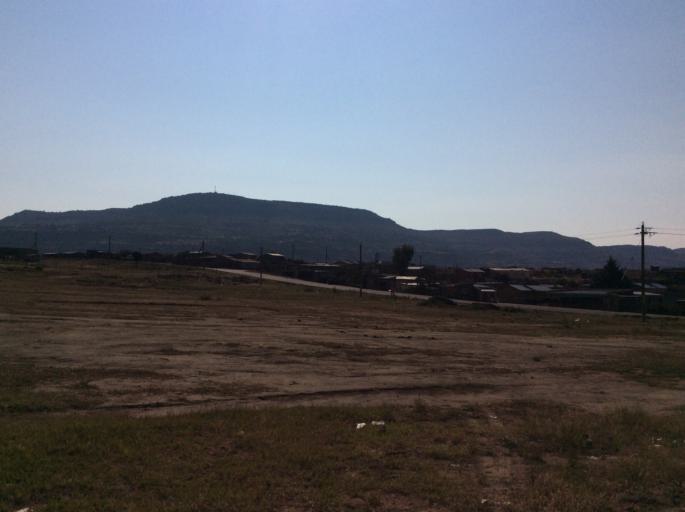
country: LS
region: Mafeteng
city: Mafeteng
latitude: -29.7210
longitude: 27.0161
